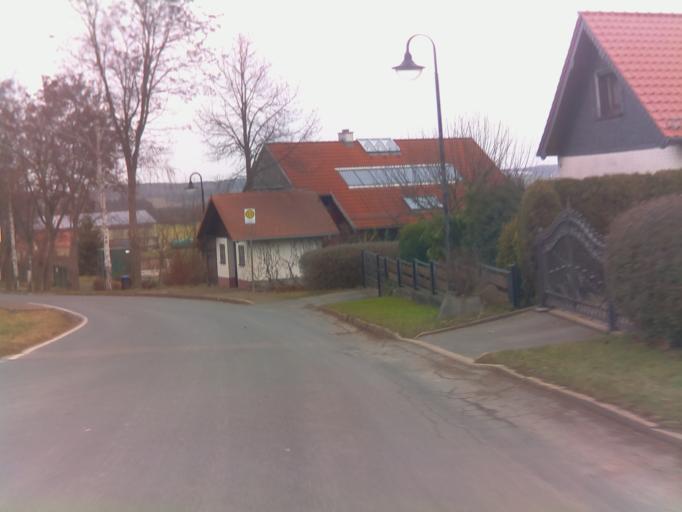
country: DE
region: Thuringia
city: Lemnitz
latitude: 50.7231
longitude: 11.8331
